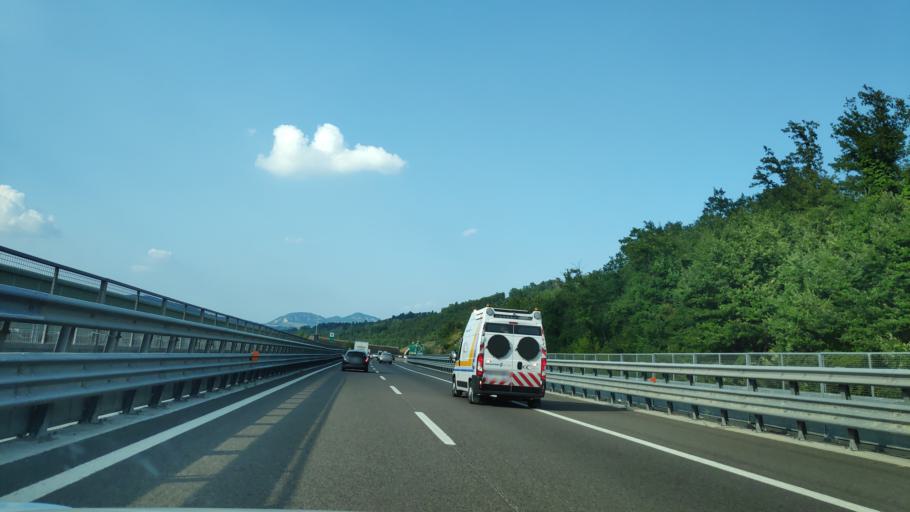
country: IT
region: Emilia-Romagna
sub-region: Provincia di Bologna
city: Grizzana
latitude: 44.2357
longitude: 11.1852
